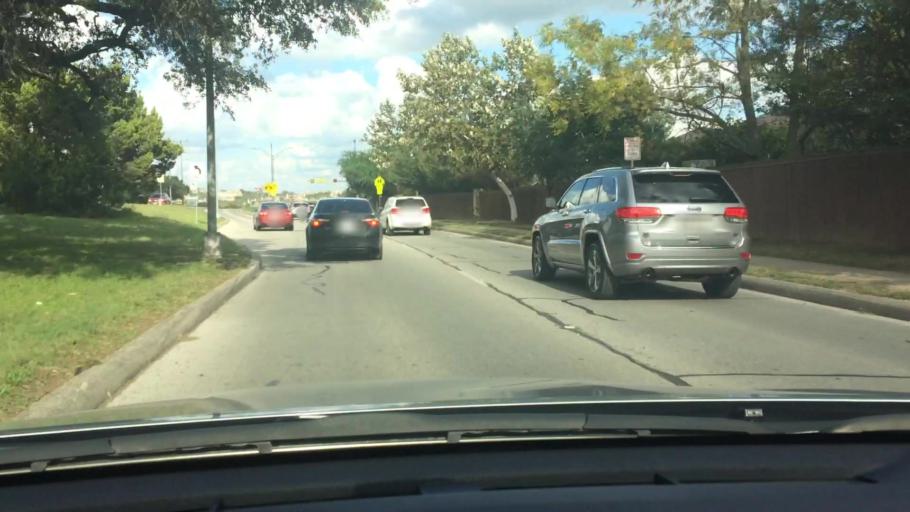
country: US
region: Texas
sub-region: Bexar County
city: Hollywood Park
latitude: 29.6394
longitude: -98.4425
